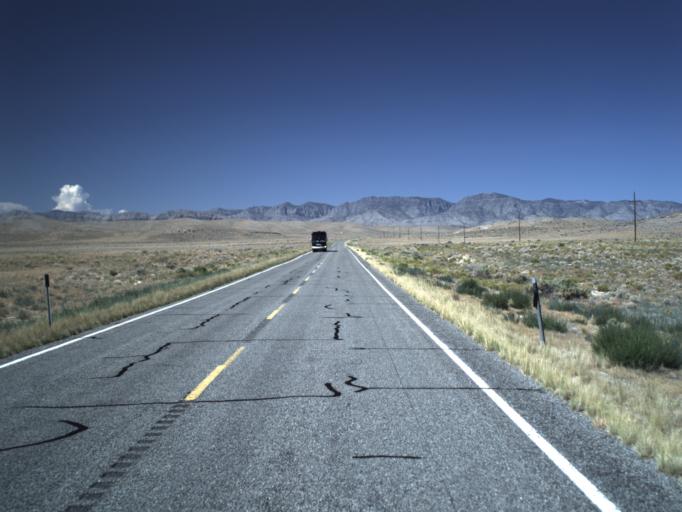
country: US
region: Utah
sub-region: Beaver County
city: Milford
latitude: 39.0438
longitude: -113.2913
